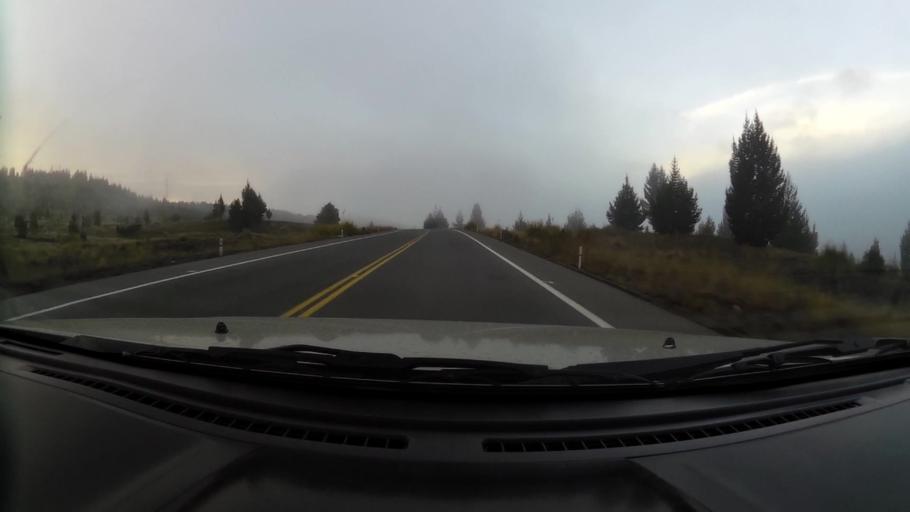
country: EC
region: Chimborazo
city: Alausi
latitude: -2.0548
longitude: -78.7438
